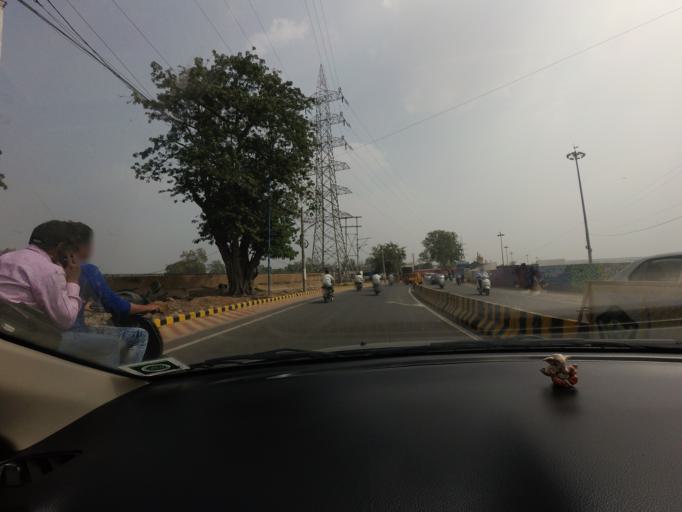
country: IN
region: Andhra Pradesh
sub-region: Krishna
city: Vijayawada
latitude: 16.5111
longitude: 80.6093
